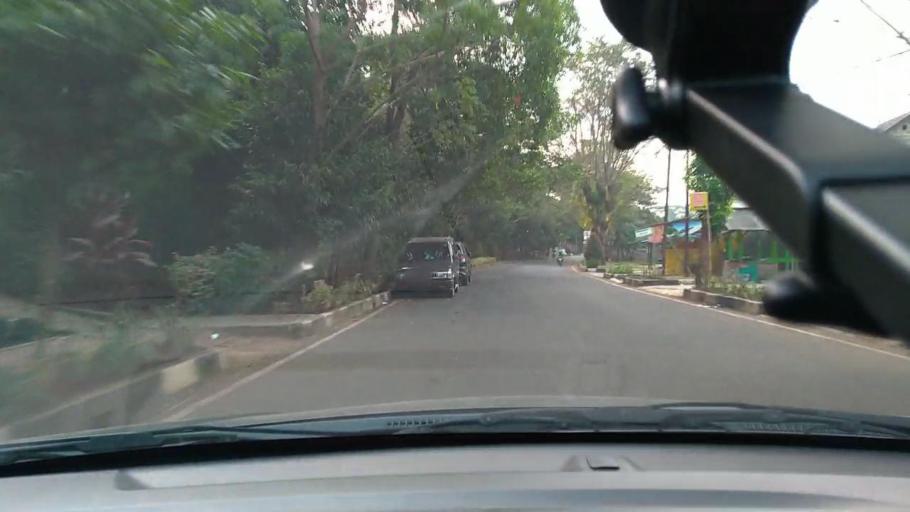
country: ID
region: West Java
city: Purwakarta
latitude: -6.5312
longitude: 107.4387
